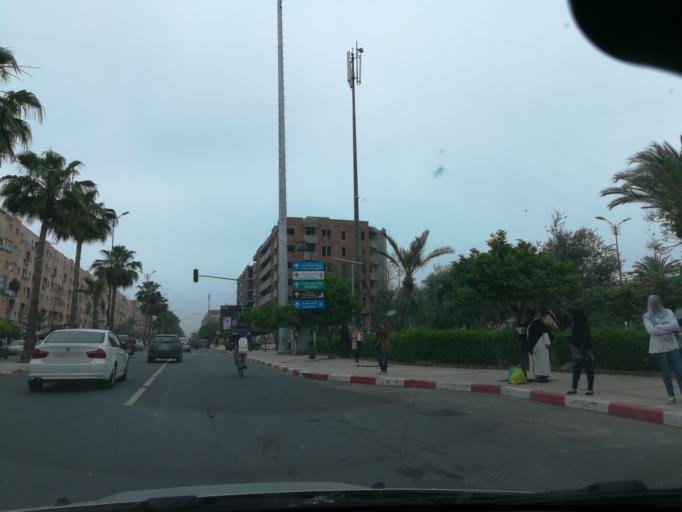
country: MA
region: Marrakech-Tensift-Al Haouz
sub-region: Marrakech
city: Marrakesh
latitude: 31.6617
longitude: -8.0075
